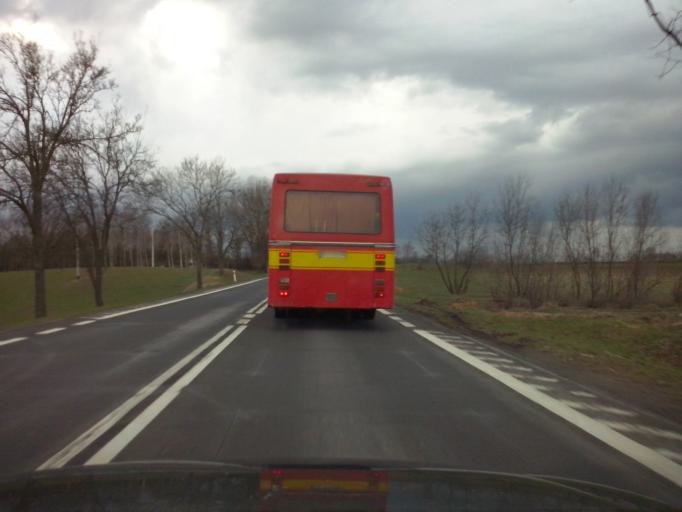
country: PL
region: Lublin Voivodeship
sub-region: Powiat chelmski
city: Rejowiec Fabryczny
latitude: 51.1725
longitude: 23.2887
